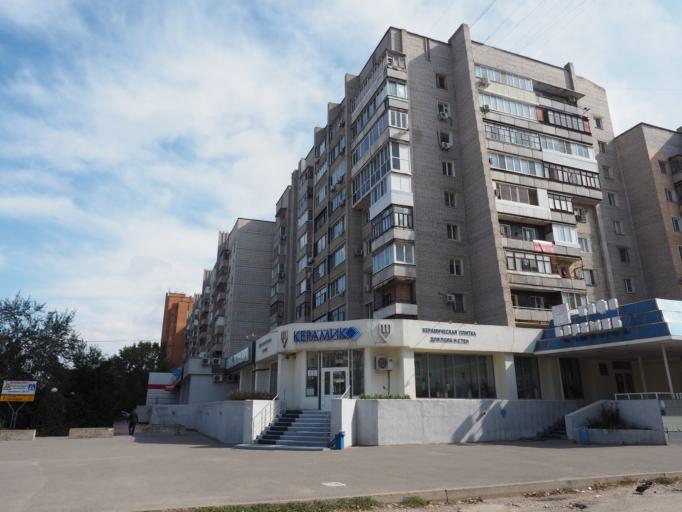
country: RU
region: Volgograd
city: Krasnoslobodsk
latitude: 48.5137
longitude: 44.5486
